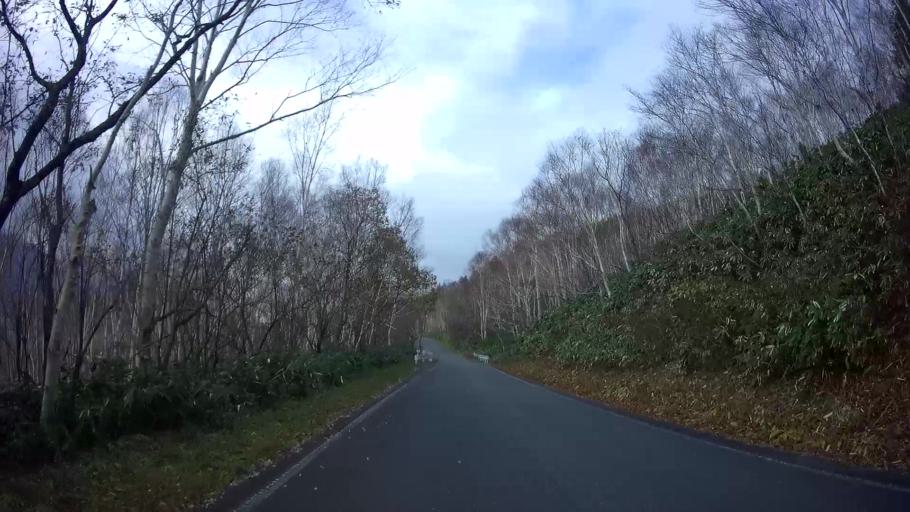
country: JP
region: Gunma
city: Nakanojomachi
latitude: 36.7029
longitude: 138.6541
